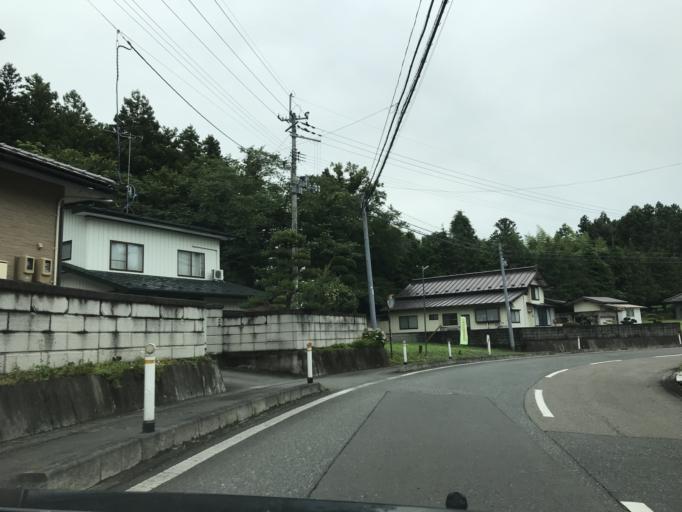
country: JP
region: Iwate
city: Ichinoseki
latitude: 38.8121
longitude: 141.1965
